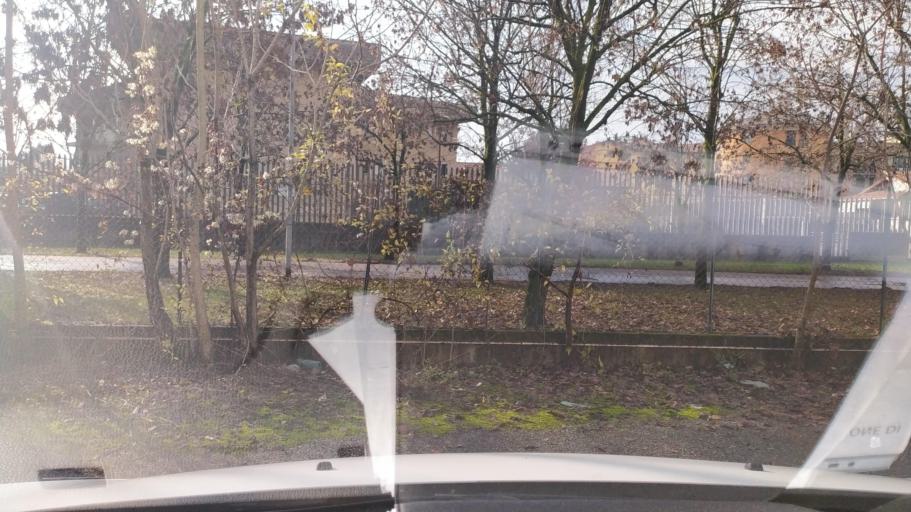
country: IT
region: Lombardy
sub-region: Provincia di Brescia
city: Palazzolo sull'Oglio
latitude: 45.5961
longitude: 9.8902
